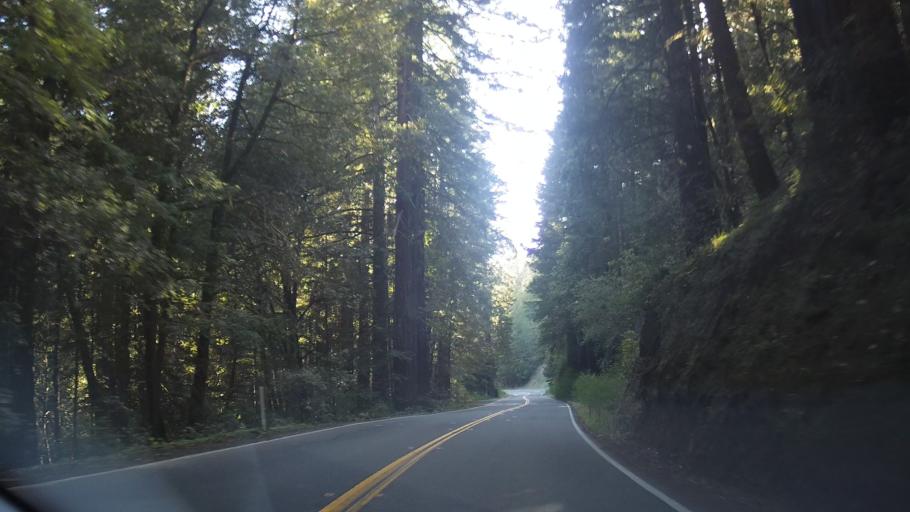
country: US
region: California
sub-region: Mendocino County
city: Brooktrails
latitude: 39.3483
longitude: -123.5174
